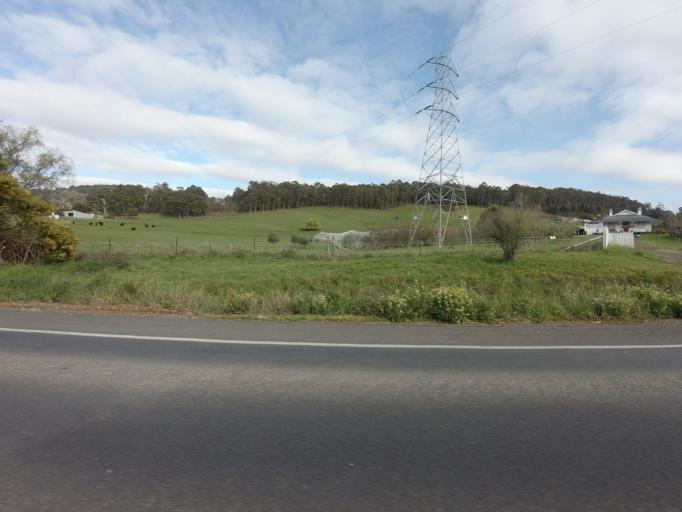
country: AU
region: Tasmania
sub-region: Huon Valley
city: Huonville
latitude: -43.0417
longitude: 147.0446
